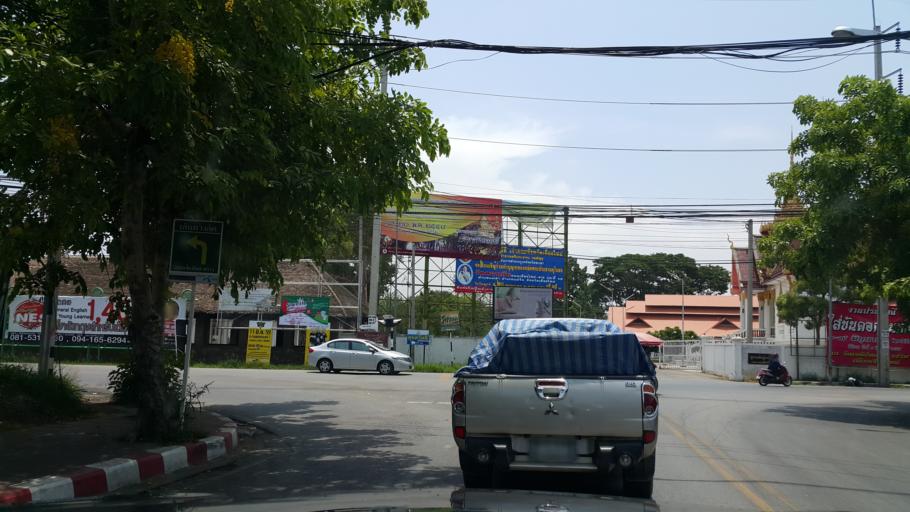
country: TH
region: Chiang Mai
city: Chiang Mai
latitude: 18.8021
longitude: 99.0119
